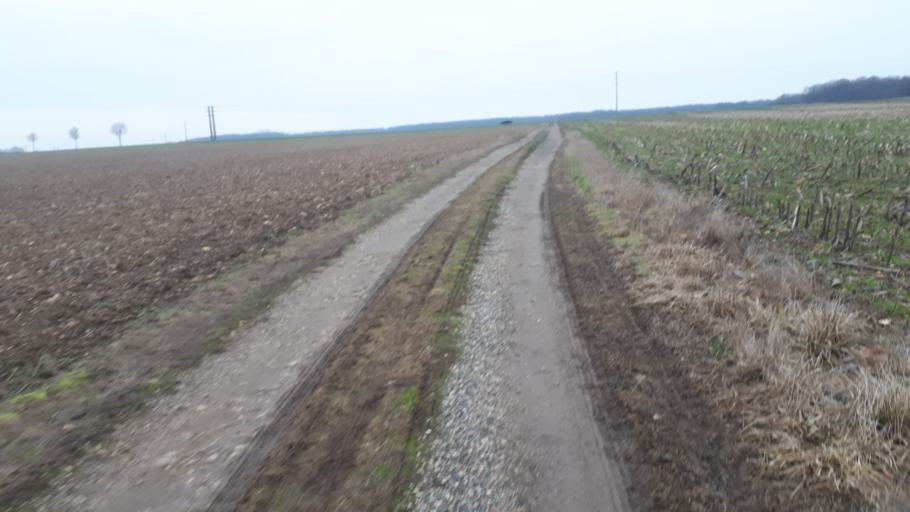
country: FR
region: Centre
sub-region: Departement du Loir-et-Cher
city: Villiers-sur-Loir
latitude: 47.8205
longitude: 1.0093
